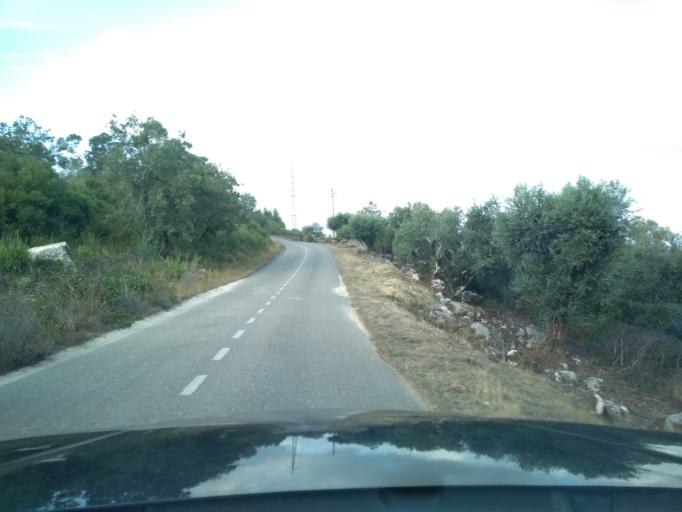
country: PT
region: Coimbra
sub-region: Condeixa-A-Nova
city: Condeixa-a-Nova
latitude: 40.0788
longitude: -8.5049
